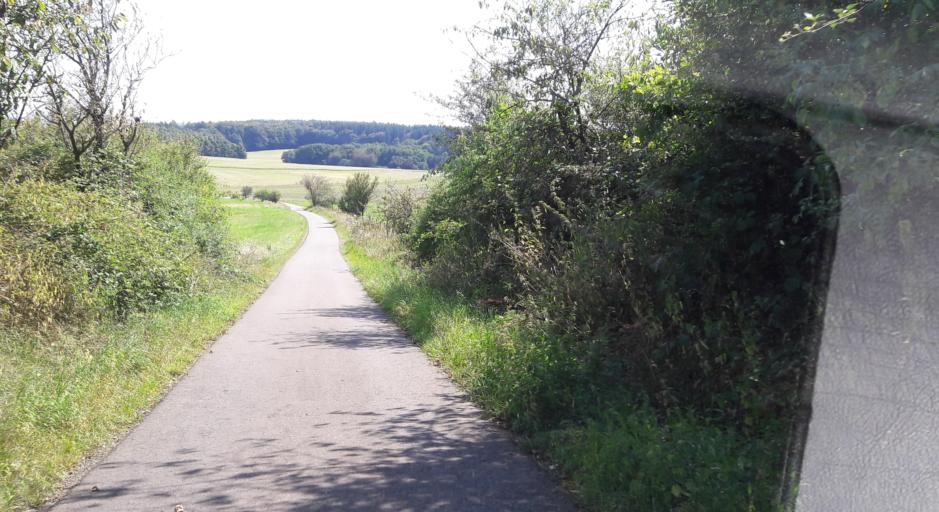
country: DE
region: Saarland
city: Mainzweiler
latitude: 49.4117
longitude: 7.1084
